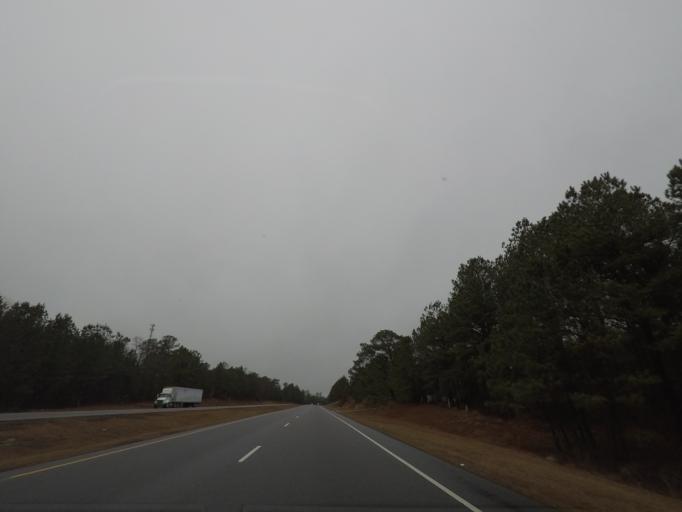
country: US
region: North Carolina
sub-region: Lee County
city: Broadway
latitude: 35.3407
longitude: -79.1016
